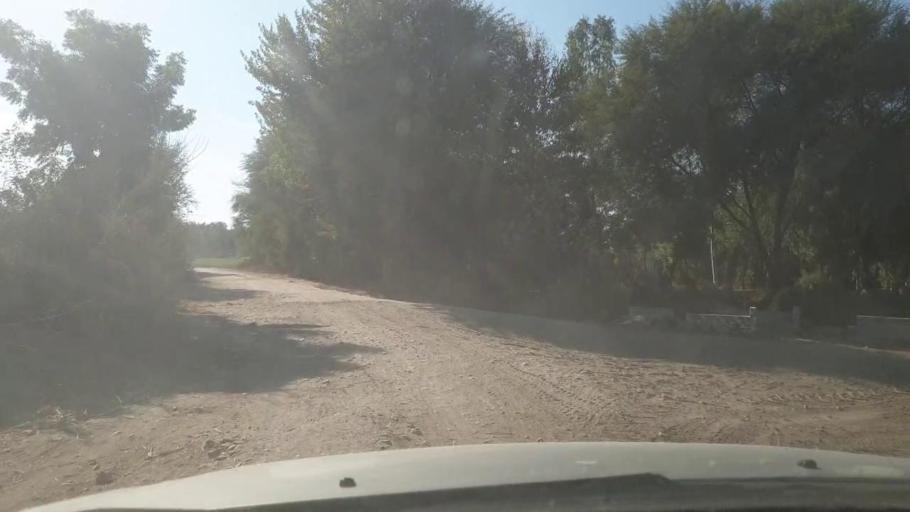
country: PK
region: Sindh
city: Ghotki
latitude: 27.9759
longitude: 69.1876
